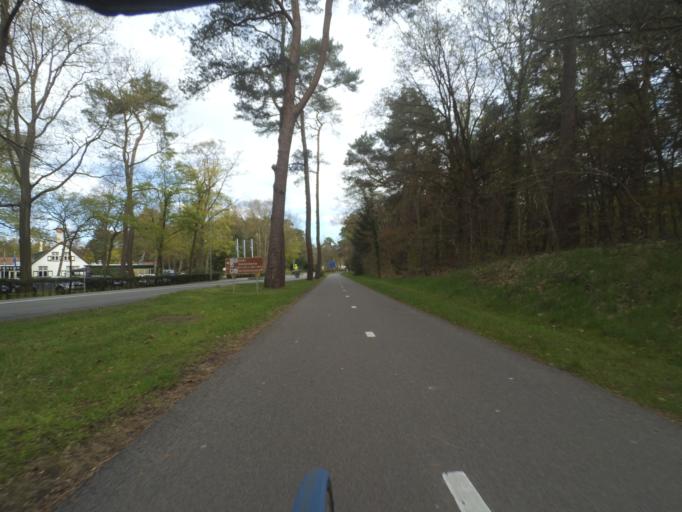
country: NL
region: Gelderland
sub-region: Gemeente Nunspeet
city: Nunspeet
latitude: 52.3673
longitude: 5.7838
